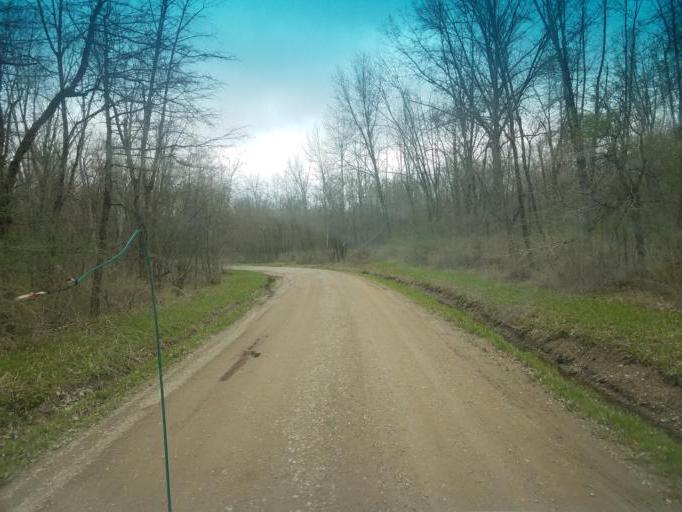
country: US
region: Ohio
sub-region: Stark County
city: Beach City
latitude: 40.6177
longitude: -81.6033
